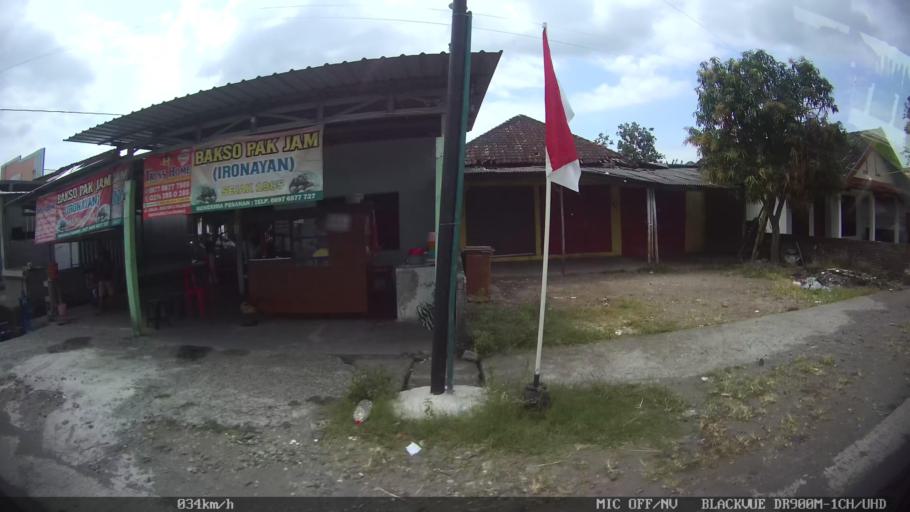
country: ID
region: Daerah Istimewa Yogyakarta
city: Depok
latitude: -7.8067
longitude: 110.4435
